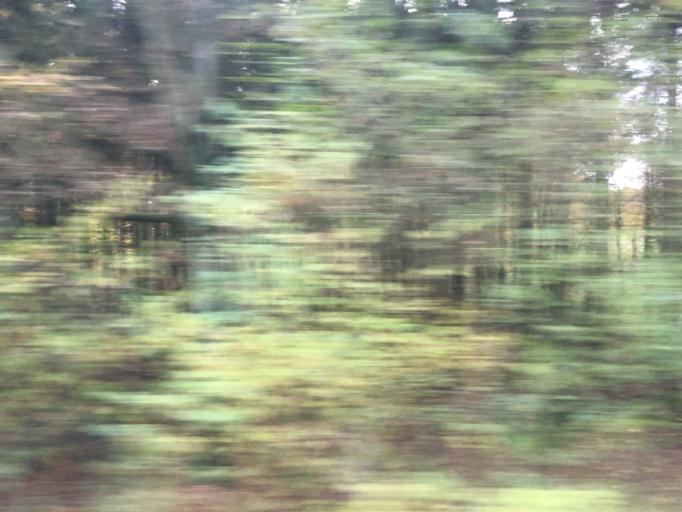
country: DE
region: North Rhine-Westphalia
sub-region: Regierungsbezirk Munster
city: Steinfurt
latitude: 52.1258
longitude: 7.3635
